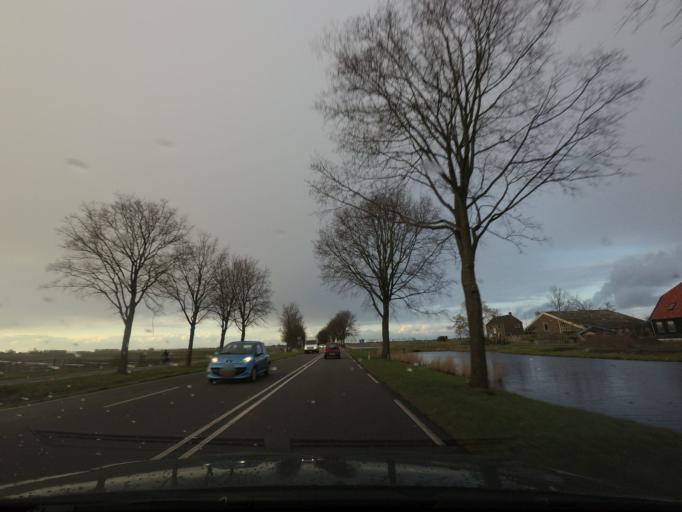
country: NL
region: North Holland
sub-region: Gemeente Edam-Volendam
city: Edam
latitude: 52.5492
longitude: 5.0197
